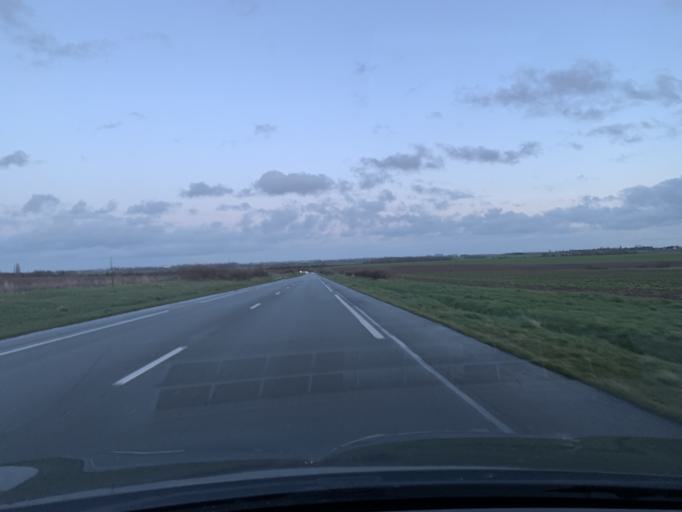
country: FR
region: Nord-Pas-de-Calais
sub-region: Departement du Nord
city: Cambrai
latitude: 50.1512
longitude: 3.2699
